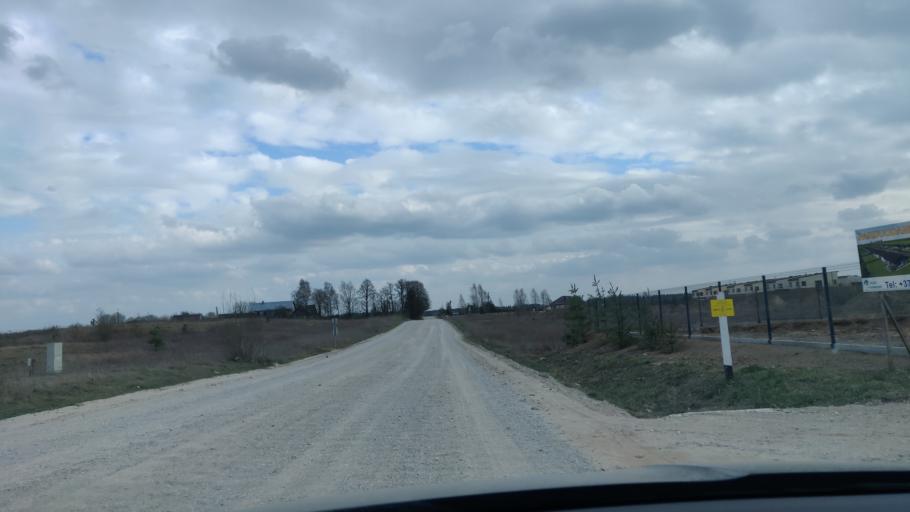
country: LT
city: Lentvaris
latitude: 54.6183
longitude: 25.0669
